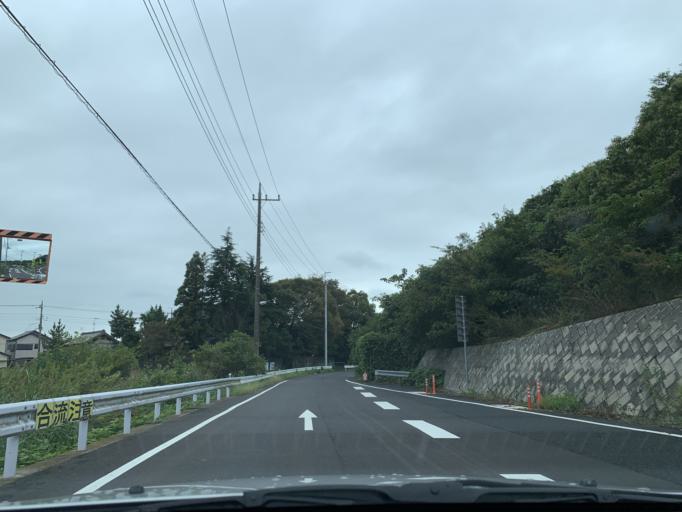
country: JP
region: Chiba
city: Nagareyama
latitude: 35.8650
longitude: 139.8844
